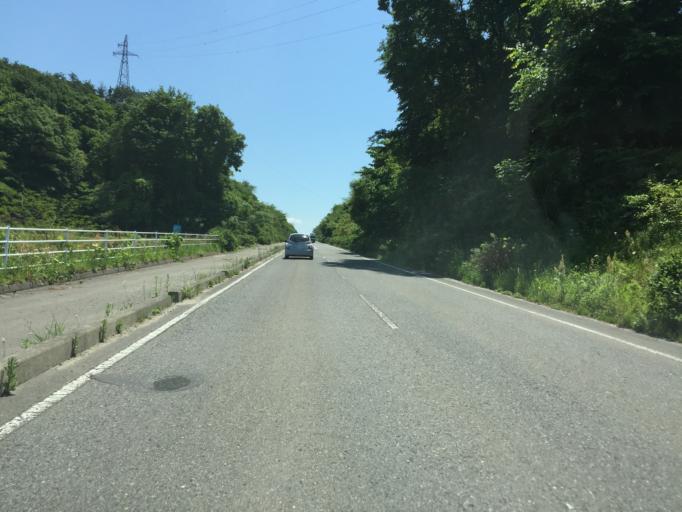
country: JP
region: Fukushima
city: Motomiya
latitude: 37.5334
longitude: 140.4218
